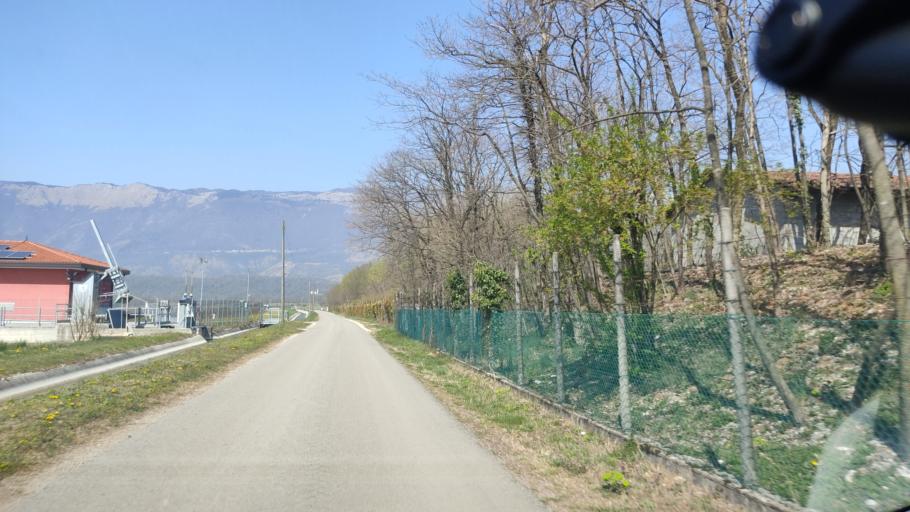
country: IT
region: Friuli Venezia Giulia
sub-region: Provincia di Pordenone
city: Vigonovo-Fontanafredda
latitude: 46.0176
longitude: 12.5499
